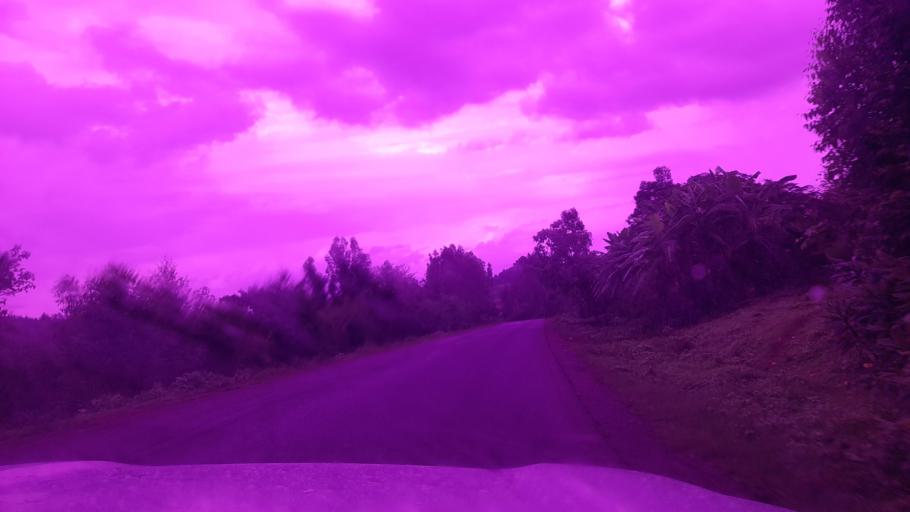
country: ET
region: Oromiya
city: Jima
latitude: 7.7102
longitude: 37.0446
